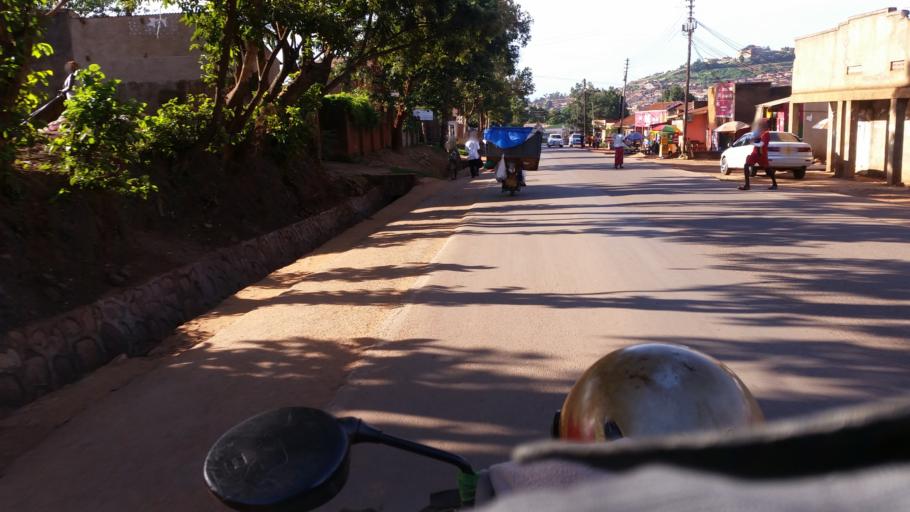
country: UG
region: Central Region
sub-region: Wakiso District
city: Kireka
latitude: 0.3254
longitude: 32.6370
